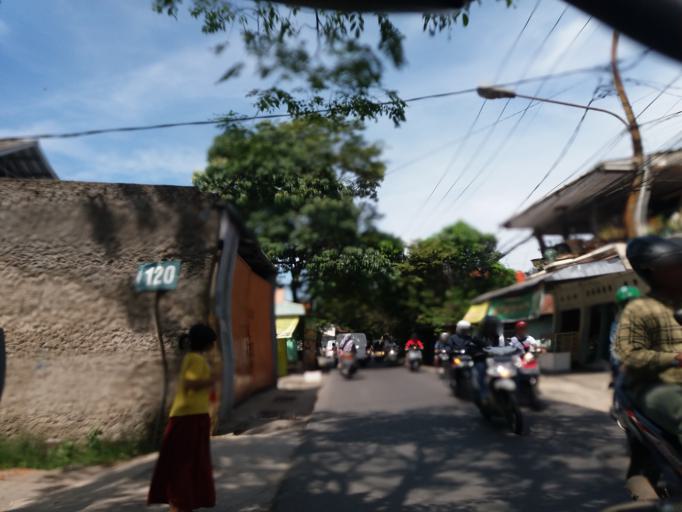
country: ID
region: West Java
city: Margahayukencana
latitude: -6.9512
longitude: 107.5767
